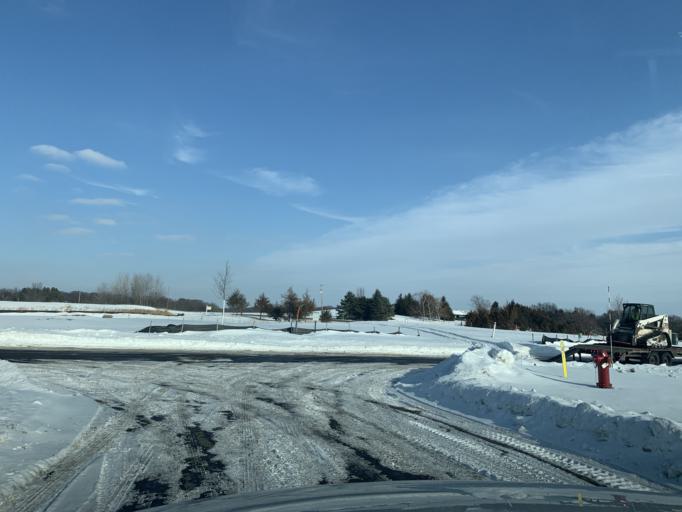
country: US
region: Minnesota
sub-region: Wright County
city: Buffalo
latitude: 45.2044
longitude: -93.8282
